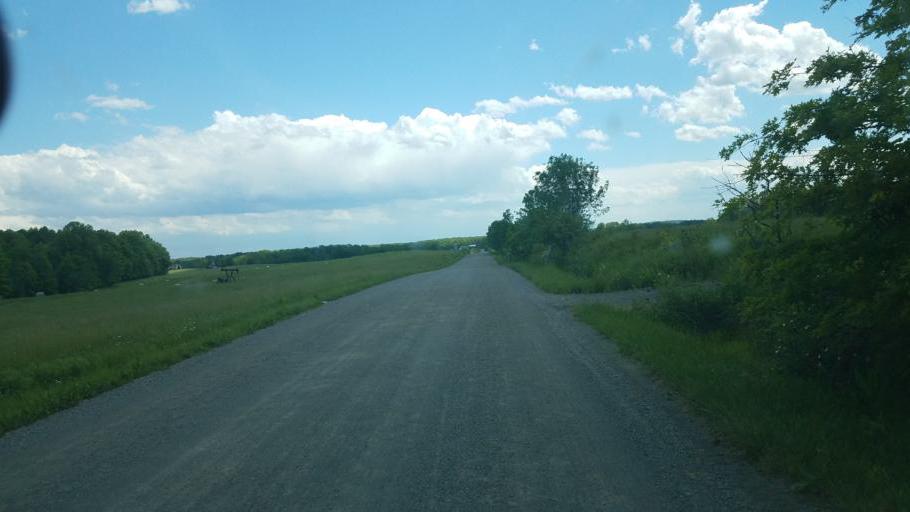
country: US
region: Ohio
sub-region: Geauga County
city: Middlefield
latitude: 41.3995
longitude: -80.9901
